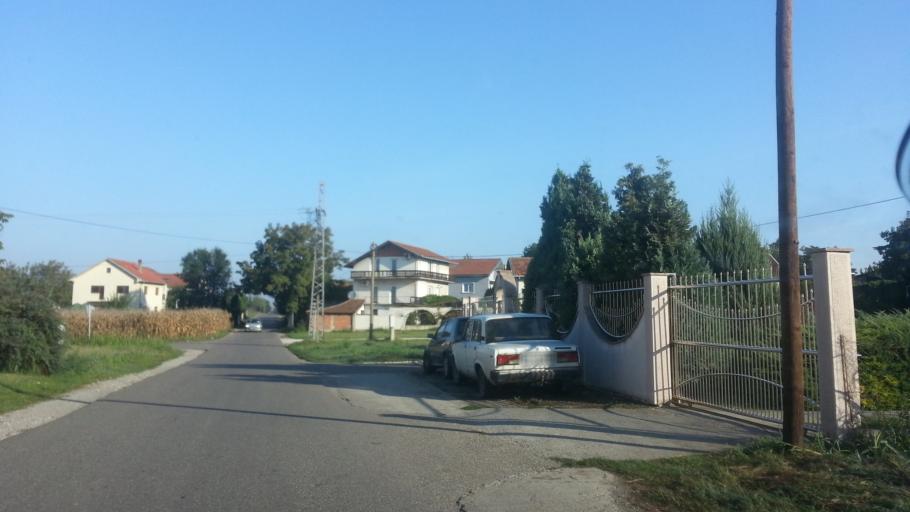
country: RS
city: Stari Banovci
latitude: 44.9704
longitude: 20.2785
